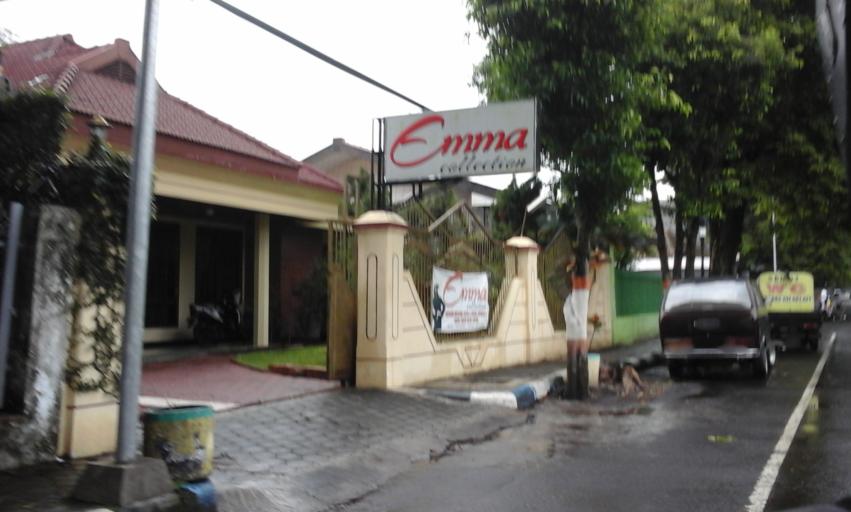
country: ID
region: East Java
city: Kadipaten
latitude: -8.1323
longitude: 113.2182
